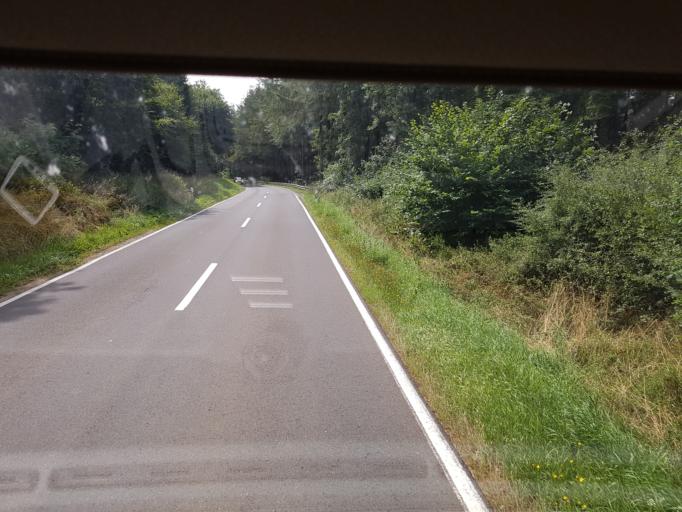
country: DE
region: Rheinland-Pfalz
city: Masthorn
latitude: 50.1723
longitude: 6.3045
